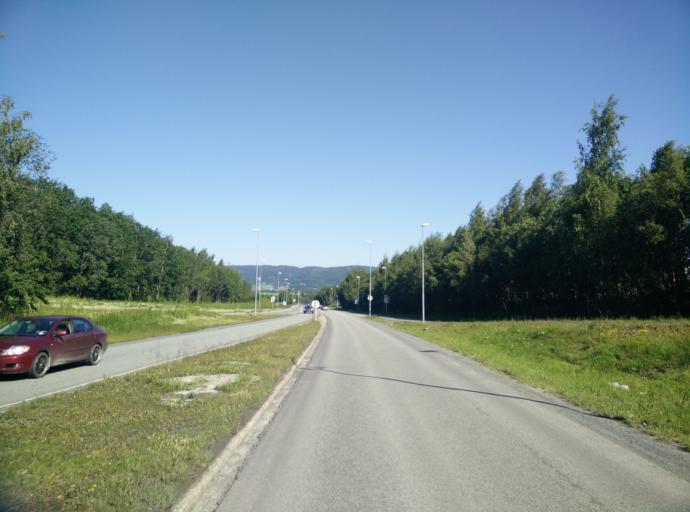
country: NO
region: Sor-Trondelag
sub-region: Trondheim
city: Trondheim
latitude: 63.3703
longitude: 10.3479
